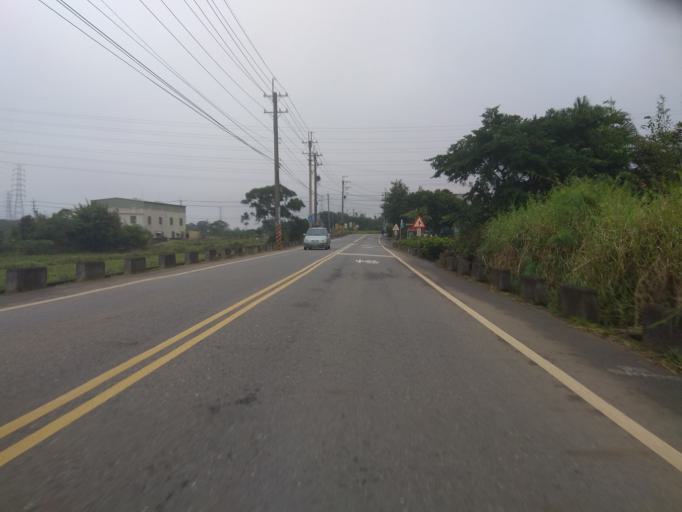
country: TW
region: Taiwan
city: Taoyuan City
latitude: 24.9910
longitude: 121.1251
